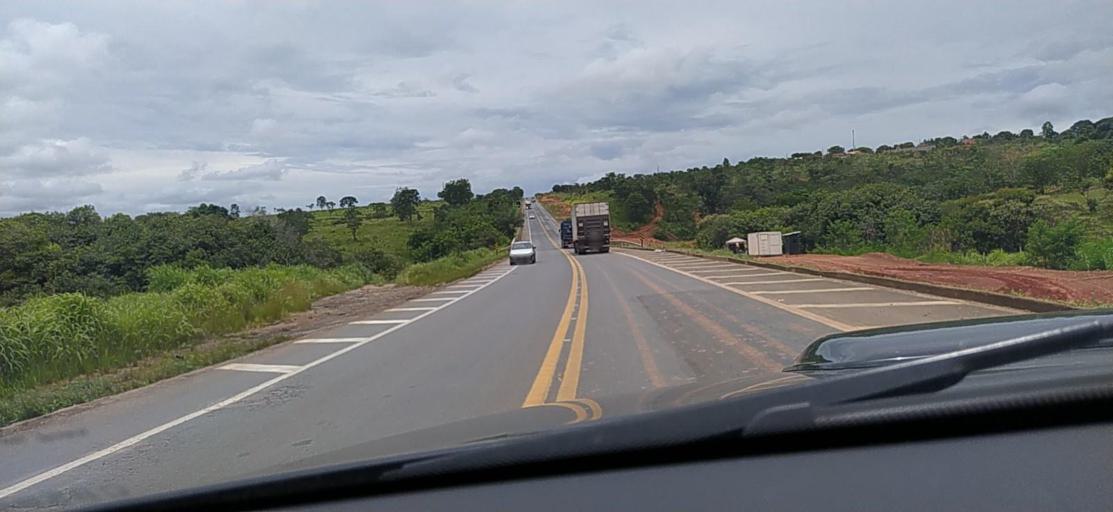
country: BR
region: Minas Gerais
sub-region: Curvelo
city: Curvelo
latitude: -18.7404
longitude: -44.4435
